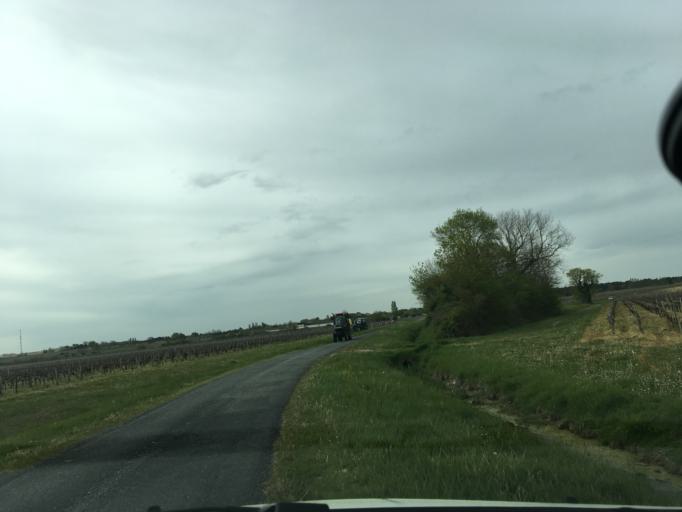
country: FR
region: Aquitaine
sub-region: Departement de la Gironde
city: Lesparre-Medoc
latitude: 45.3226
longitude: -0.8953
